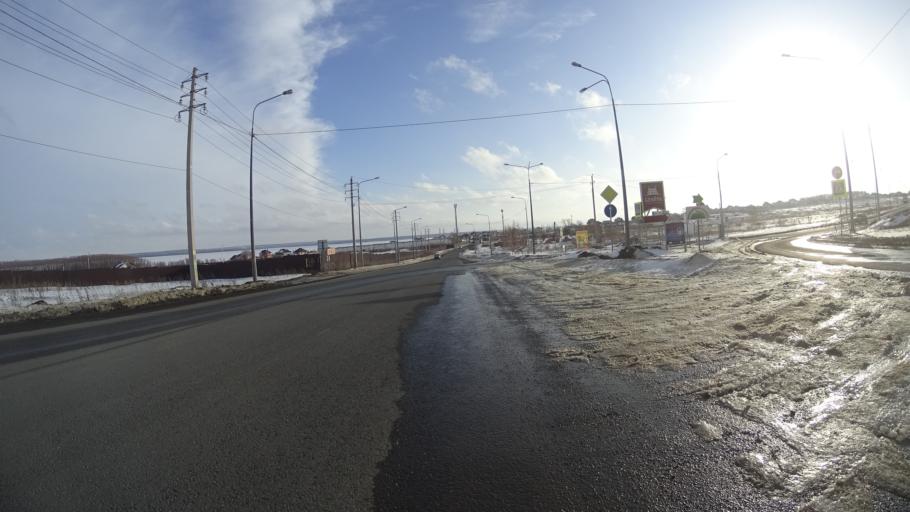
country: RU
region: Chelyabinsk
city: Sargazy
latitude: 55.1215
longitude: 61.2870
